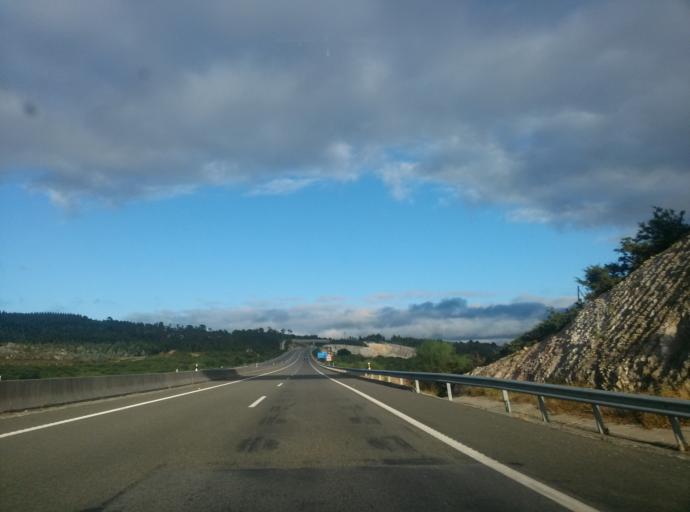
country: ES
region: Galicia
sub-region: Provincia de Lugo
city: Vilalba
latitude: 43.3602
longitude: -7.7637
